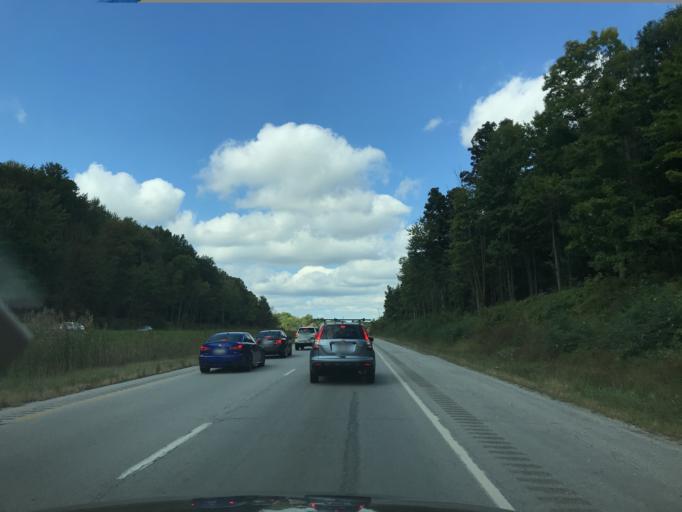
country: US
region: Ohio
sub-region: Summit County
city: Twinsburg
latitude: 41.3202
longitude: -81.4641
